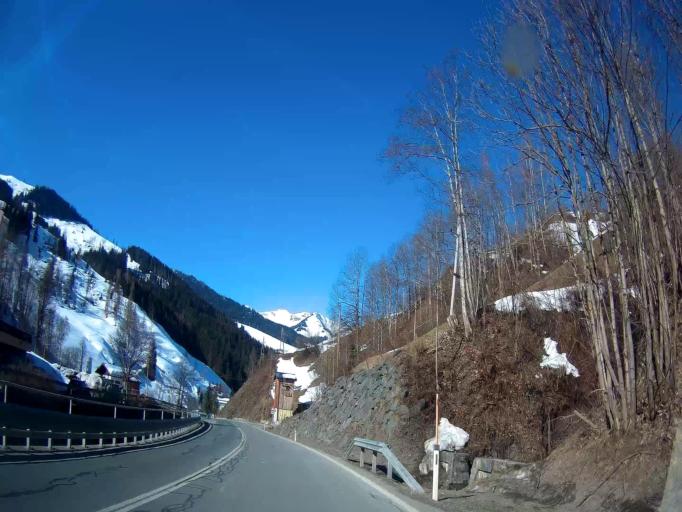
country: AT
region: Salzburg
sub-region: Politischer Bezirk Zell am See
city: Maria Alm am Steinernen Meer
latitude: 47.3873
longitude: 12.9372
